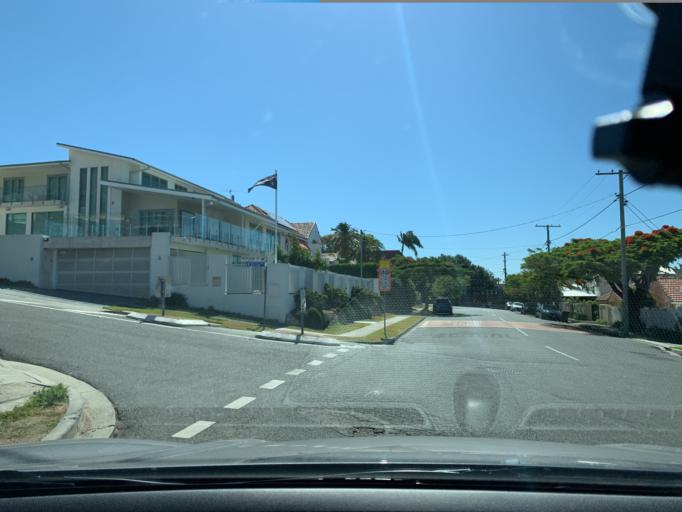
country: AU
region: Queensland
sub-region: Brisbane
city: Ascot
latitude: -27.4303
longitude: 153.0516
